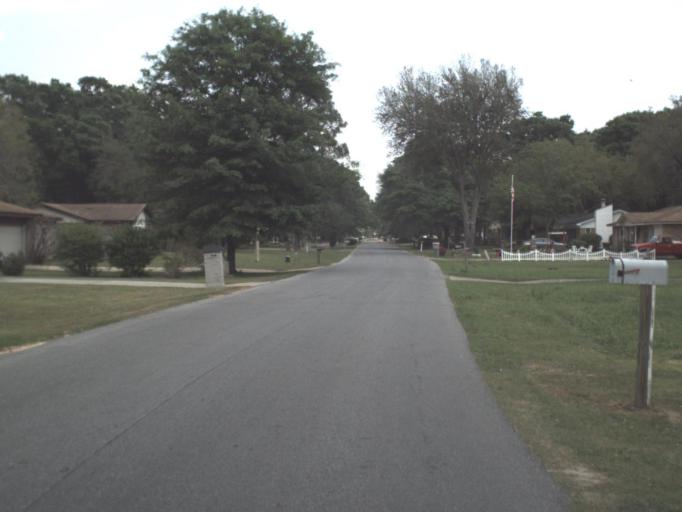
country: US
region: Florida
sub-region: Santa Rosa County
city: Point Baker
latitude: 30.6664
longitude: -87.0525
